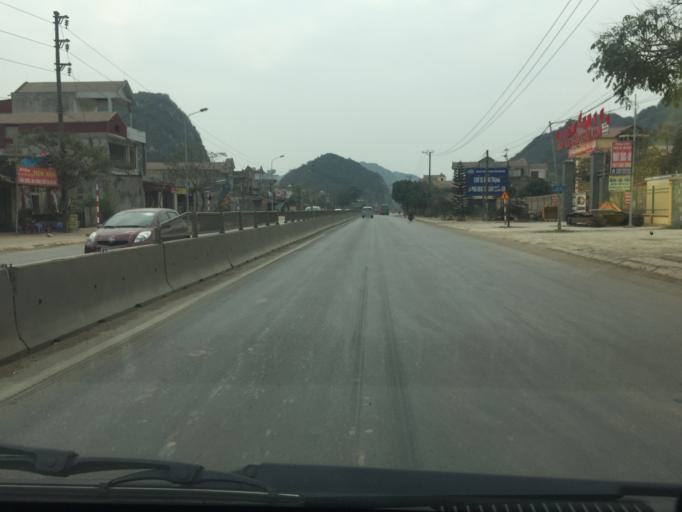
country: VN
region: Ninh Binh
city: Thi Tran Tam Diep
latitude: 20.1352
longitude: 105.8711
